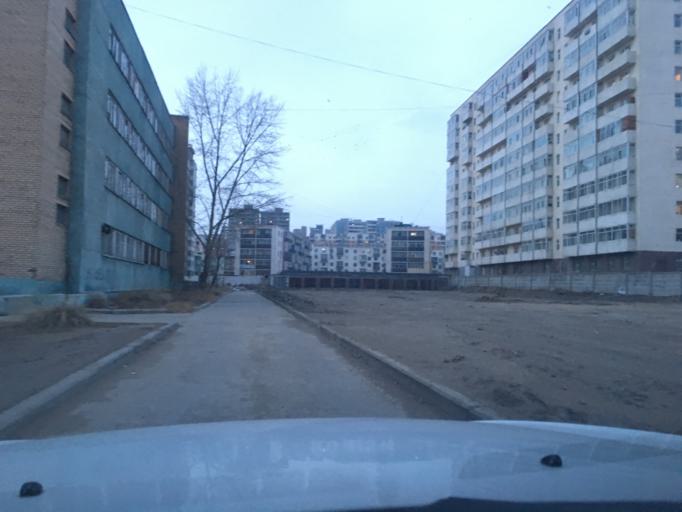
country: MN
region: Ulaanbaatar
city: Ulaanbaatar
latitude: 47.9150
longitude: 106.8612
